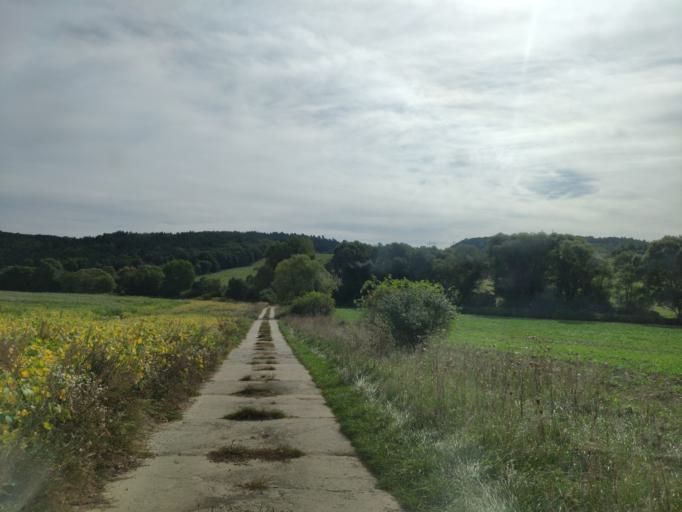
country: SK
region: Kosicky
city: Kosice
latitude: 48.8160
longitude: 21.3364
